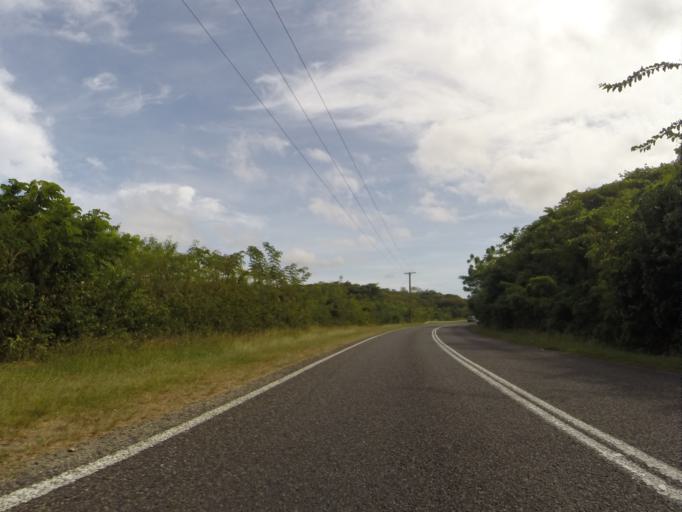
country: FJ
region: Western
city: Nadi
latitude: -18.1478
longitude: 177.4340
